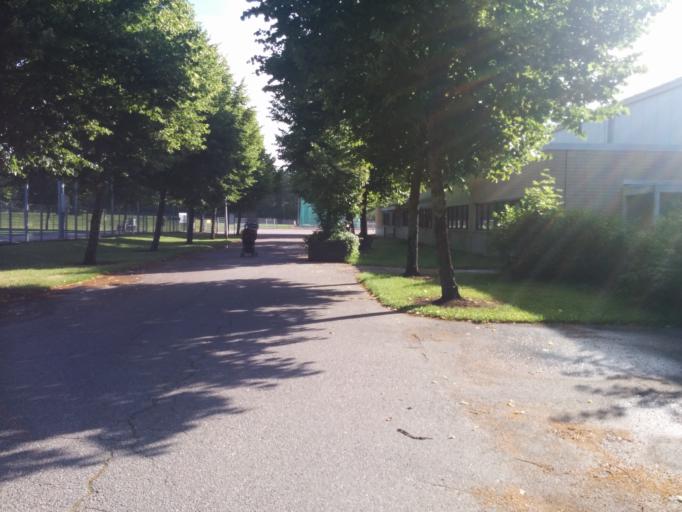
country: FI
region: Uusimaa
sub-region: Helsinki
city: Kerava
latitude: 60.4097
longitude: 25.0923
